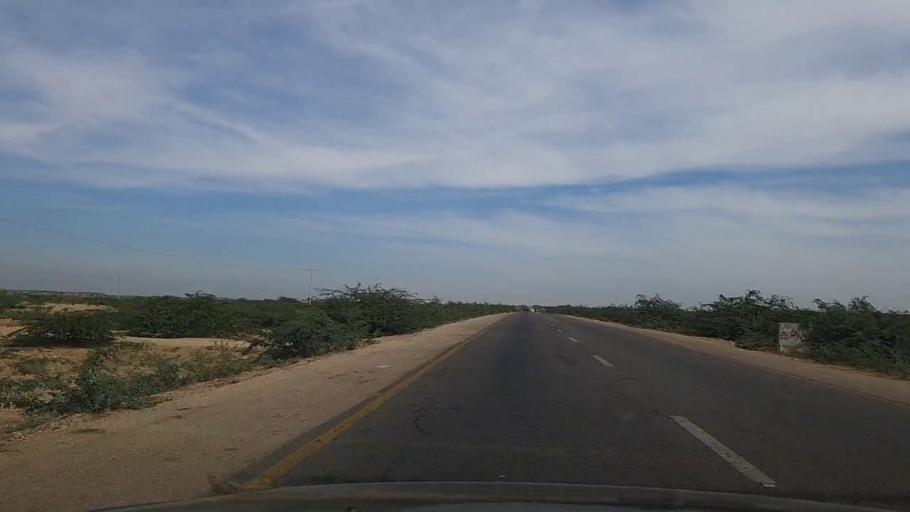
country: PK
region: Sindh
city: Thatta
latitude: 24.8420
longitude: 68.0069
